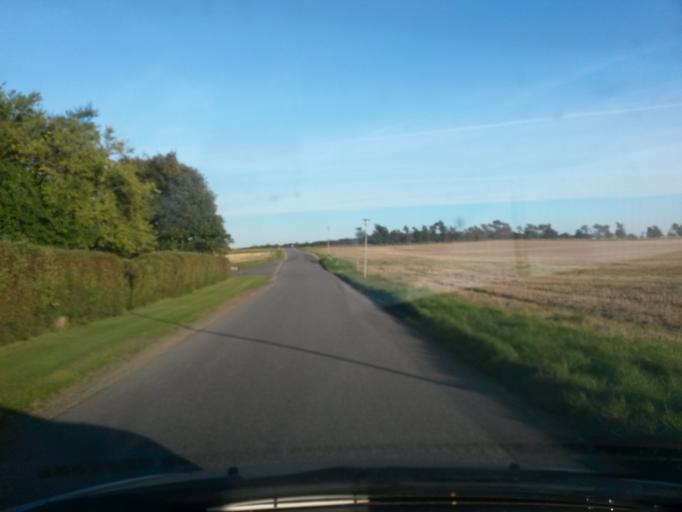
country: DK
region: Central Jutland
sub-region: Silkeborg Kommune
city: Kjellerup
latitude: 56.3260
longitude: 9.3744
